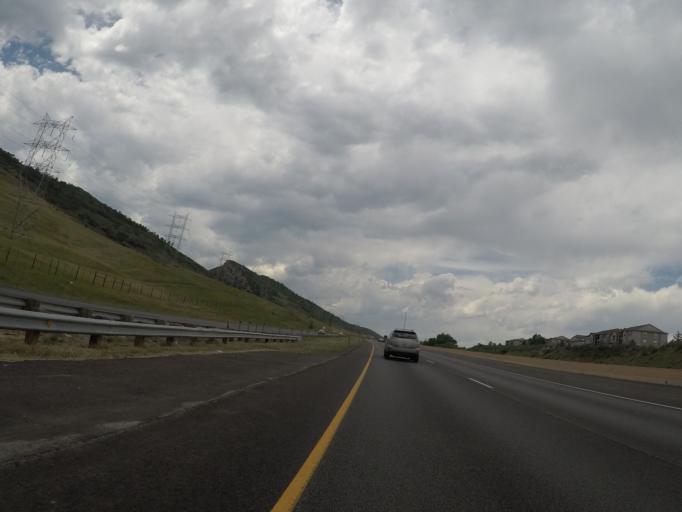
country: US
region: Colorado
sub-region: Jefferson County
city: Ken Caryl
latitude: 39.5960
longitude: -105.1499
